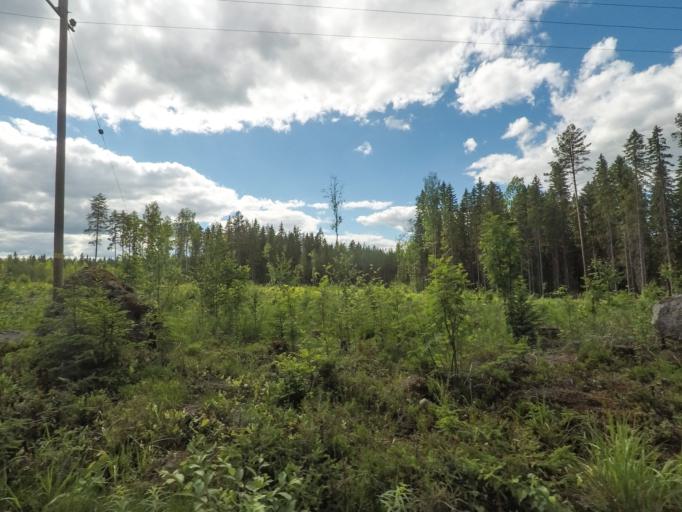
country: FI
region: Central Finland
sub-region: Jyvaeskylae
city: Hankasalmi
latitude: 62.4061
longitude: 26.6542
